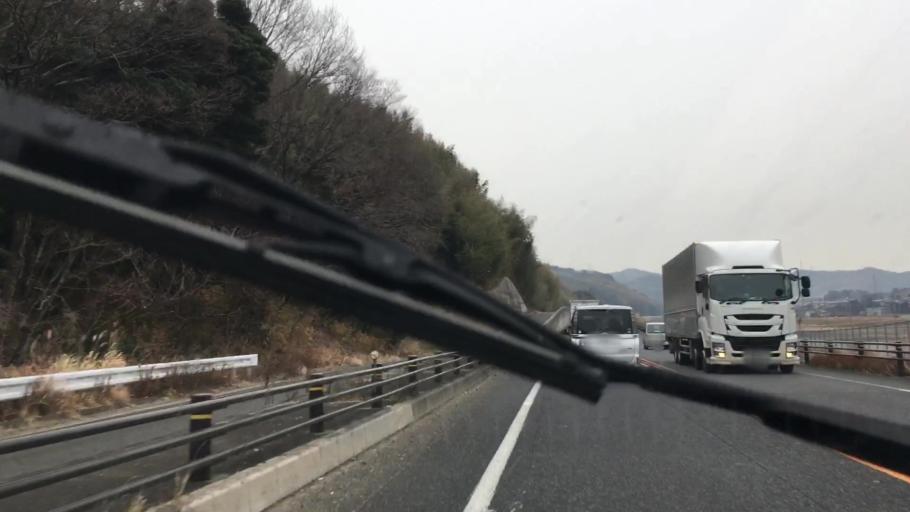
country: JP
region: Aichi
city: Nishio
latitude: 34.8613
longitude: 137.1160
